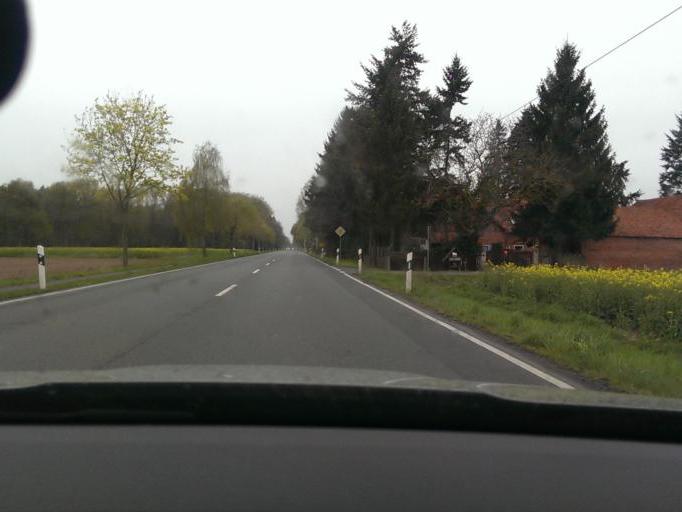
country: DE
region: Lower Saxony
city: Gilten
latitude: 52.6795
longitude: 9.5642
